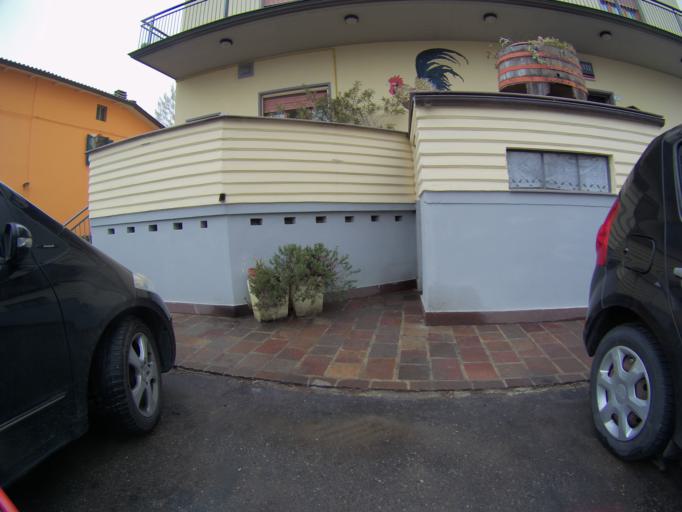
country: IT
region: Emilia-Romagna
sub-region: Provincia di Reggio Emilia
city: Ciano d'Enza
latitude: 44.5360
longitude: 10.4158
